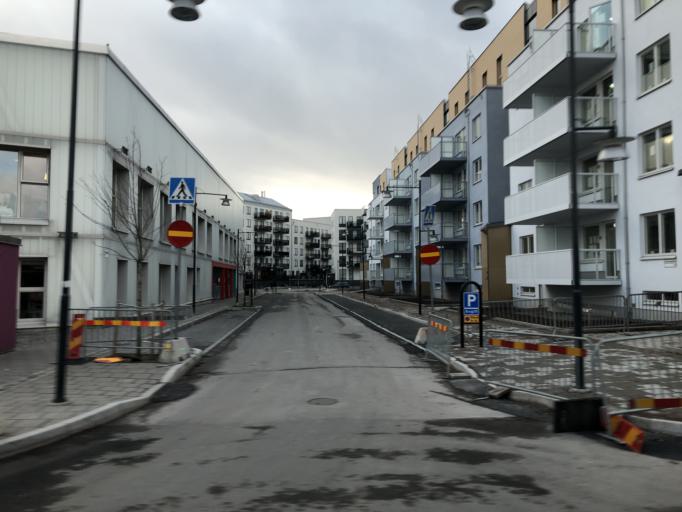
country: SE
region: Stockholm
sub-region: Jarfalla Kommun
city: Jakobsberg
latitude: 59.4135
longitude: 17.8700
